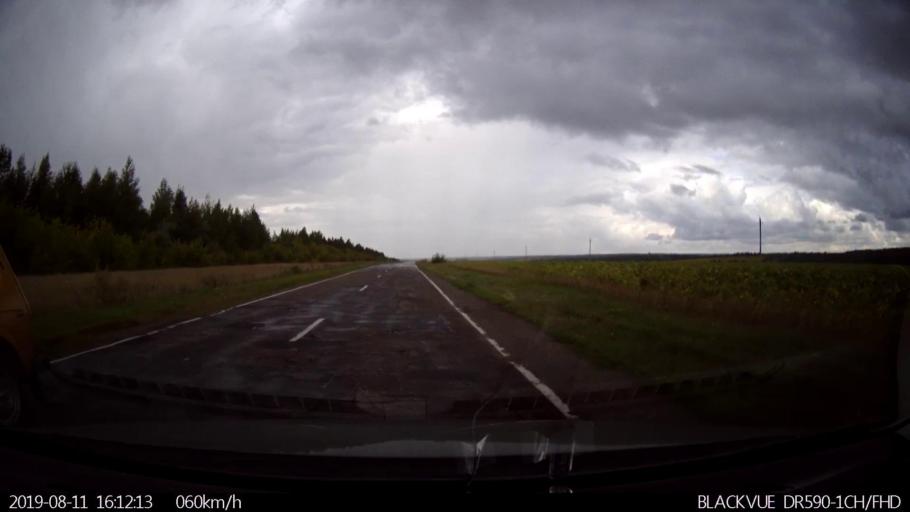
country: RU
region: Ulyanovsk
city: Ignatovka
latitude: 54.0096
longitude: 47.6412
